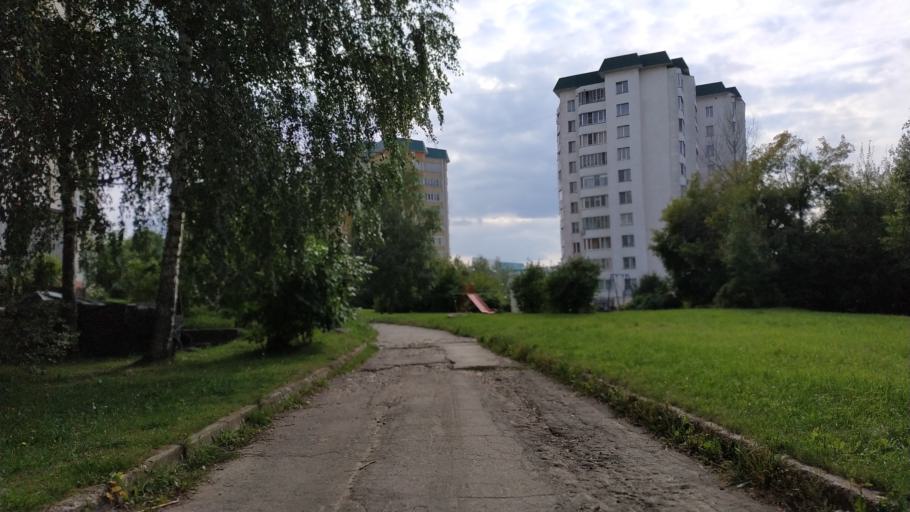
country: RU
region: Chuvashia
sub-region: Cheboksarskiy Rayon
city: Cheboksary
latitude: 56.1495
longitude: 47.2158
